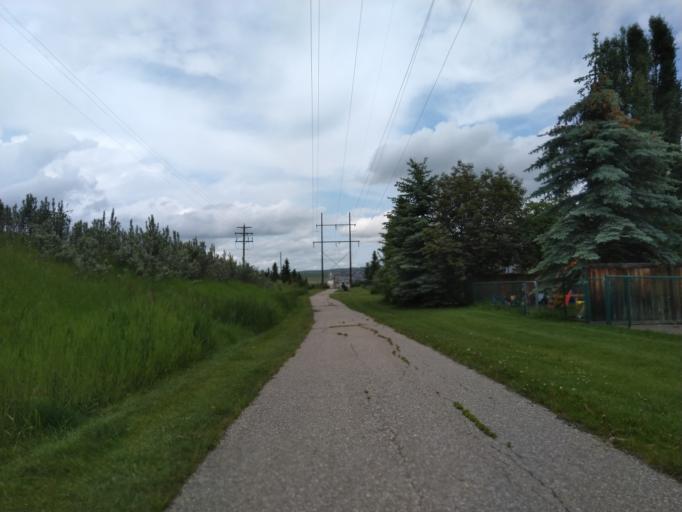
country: CA
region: Alberta
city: Cochrane
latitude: 51.1884
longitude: -114.5132
